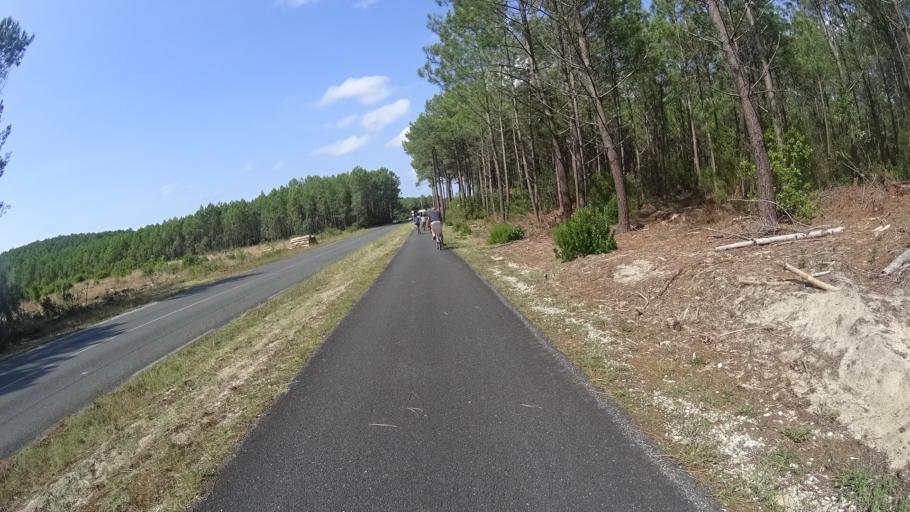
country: FR
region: Aquitaine
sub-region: Departement de la Gironde
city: Lacanau
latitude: 44.9842
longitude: -1.1438
